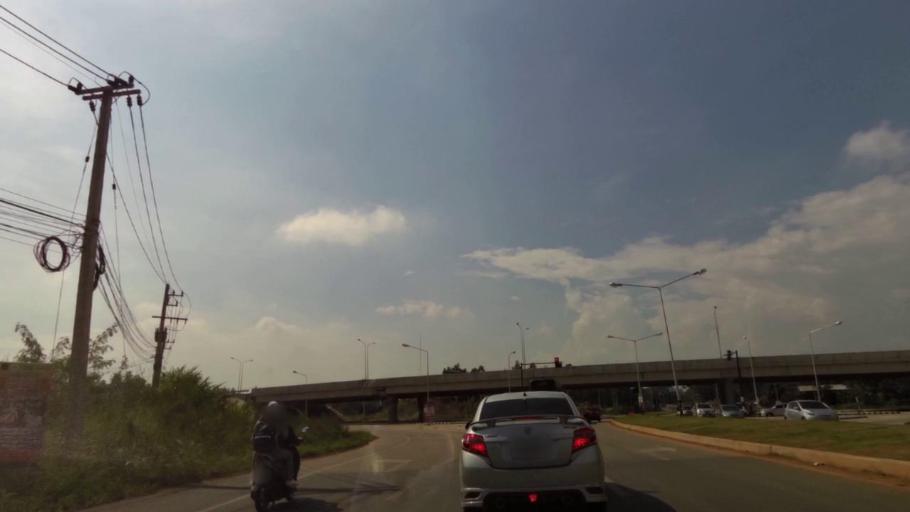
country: TH
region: Chiang Rai
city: Chiang Rai
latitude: 19.8758
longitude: 99.7870
